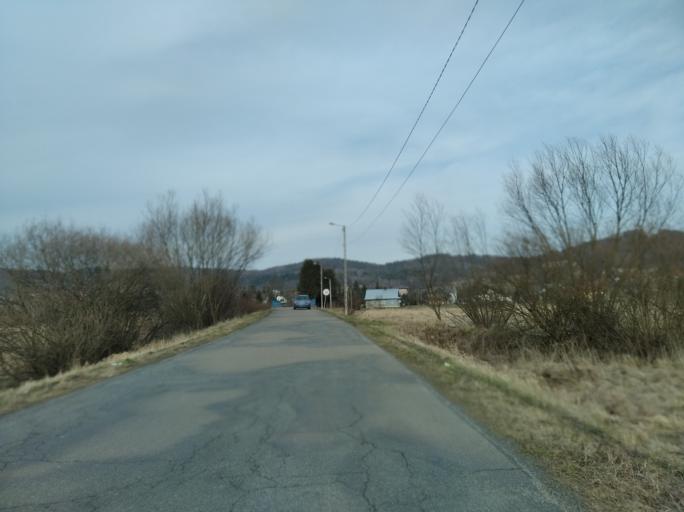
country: PL
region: Subcarpathian Voivodeship
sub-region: Powiat brzozowski
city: Blizne
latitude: 49.7504
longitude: 21.9702
